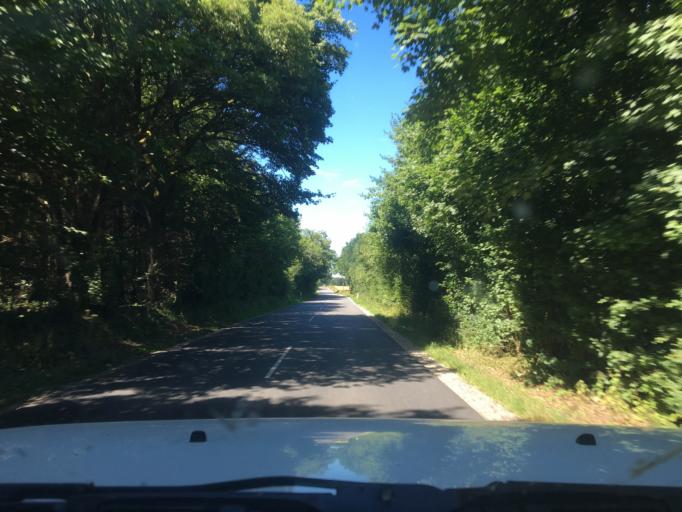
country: DK
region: Central Jutland
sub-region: Syddjurs Kommune
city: Hornslet
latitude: 56.3274
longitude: 10.3565
